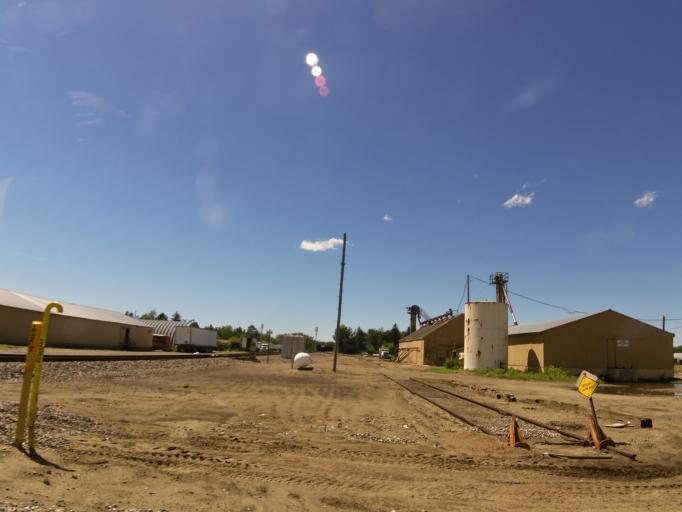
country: US
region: Minnesota
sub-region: Todd County
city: Staples
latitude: 46.3383
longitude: -94.6459
